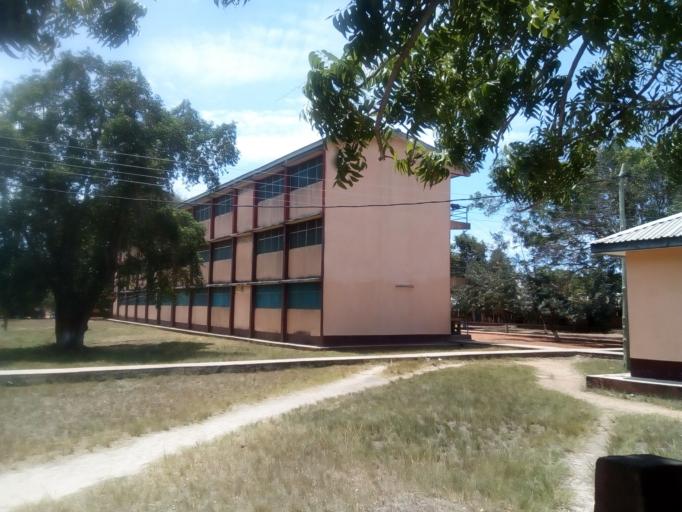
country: GH
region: Volta
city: Anloga
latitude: 5.8032
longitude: 0.6164
